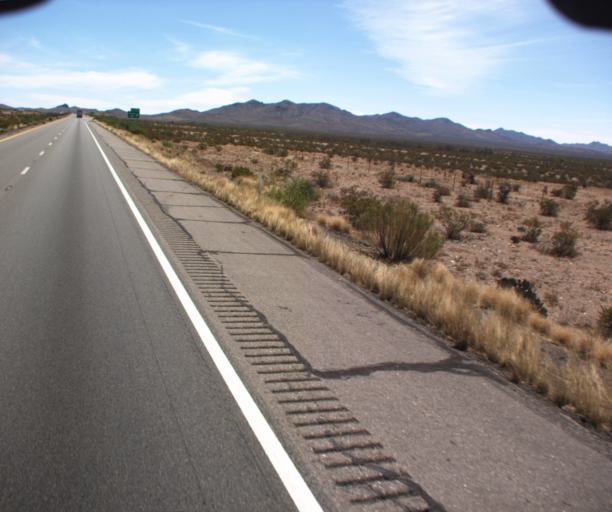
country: US
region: New Mexico
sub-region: Hidalgo County
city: Lordsburg
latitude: 32.2306
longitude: -109.0623
